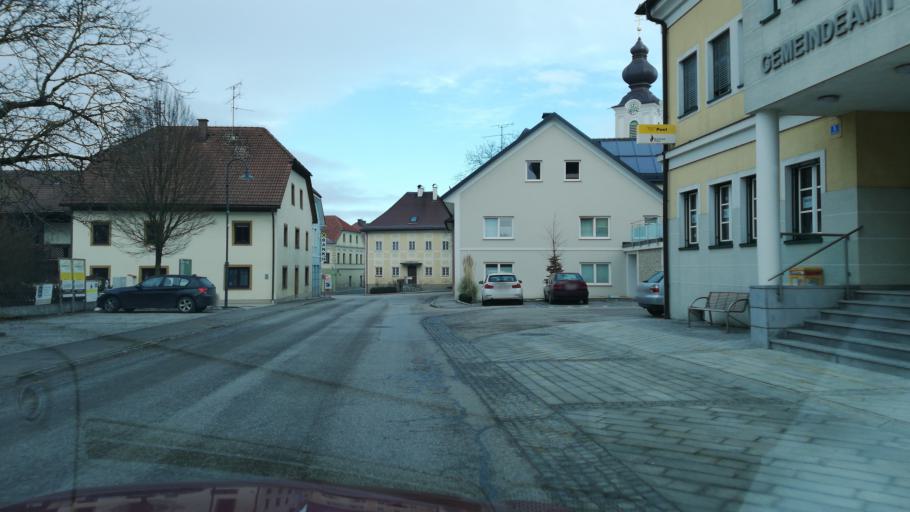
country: AT
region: Upper Austria
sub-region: Politischer Bezirk Vocklabruck
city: Wolfsegg am Hausruck
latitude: 48.1840
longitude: 13.7018
